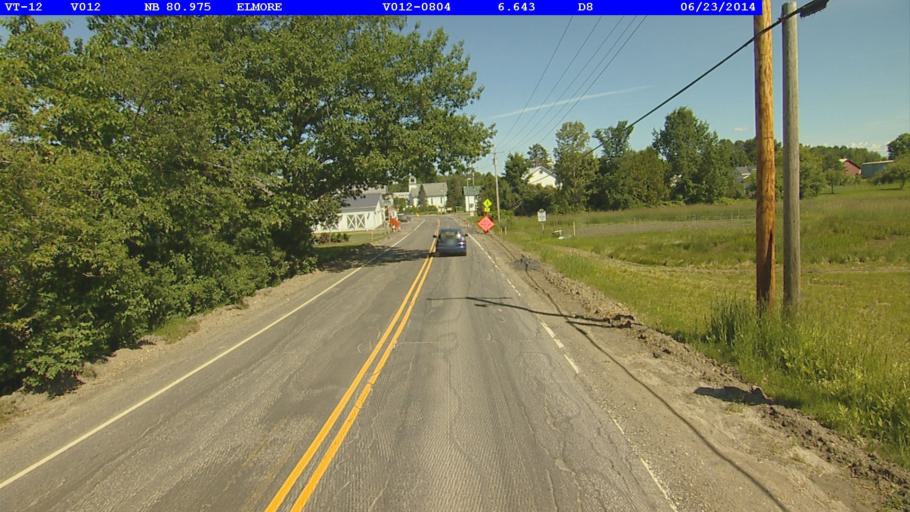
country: US
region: Vermont
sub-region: Lamoille County
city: Morrisville
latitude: 44.5395
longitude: -72.5223
